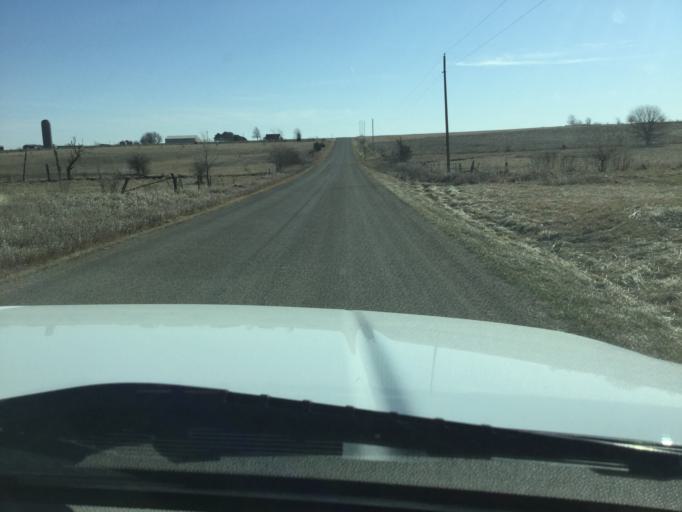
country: US
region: Kansas
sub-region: Brown County
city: Horton
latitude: 39.7255
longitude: -95.4574
